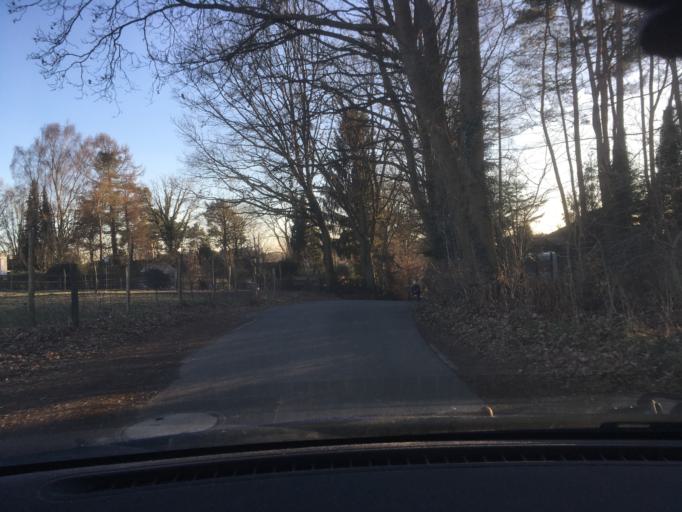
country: DE
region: Lower Saxony
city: Seevetal
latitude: 53.4015
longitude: 9.9621
